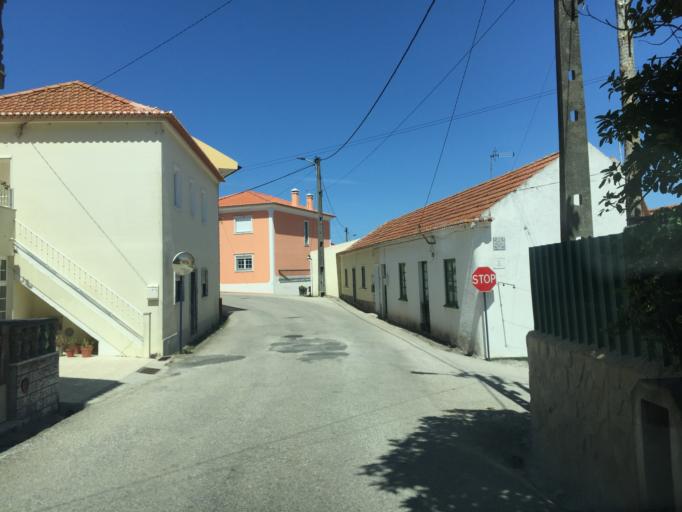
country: PT
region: Lisbon
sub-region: Lourinha
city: Lourinha
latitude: 39.2038
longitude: -9.3327
